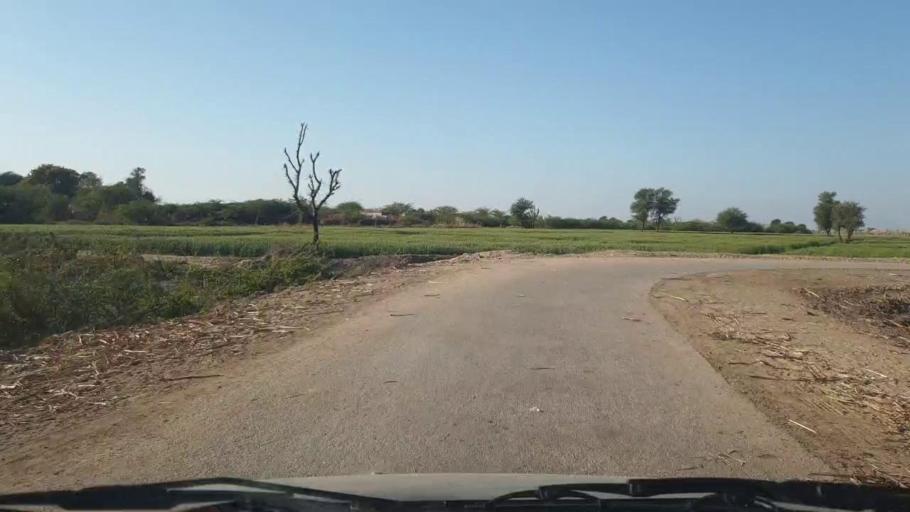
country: PK
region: Sindh
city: Samaro
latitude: 25.3487
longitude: 69.2982
